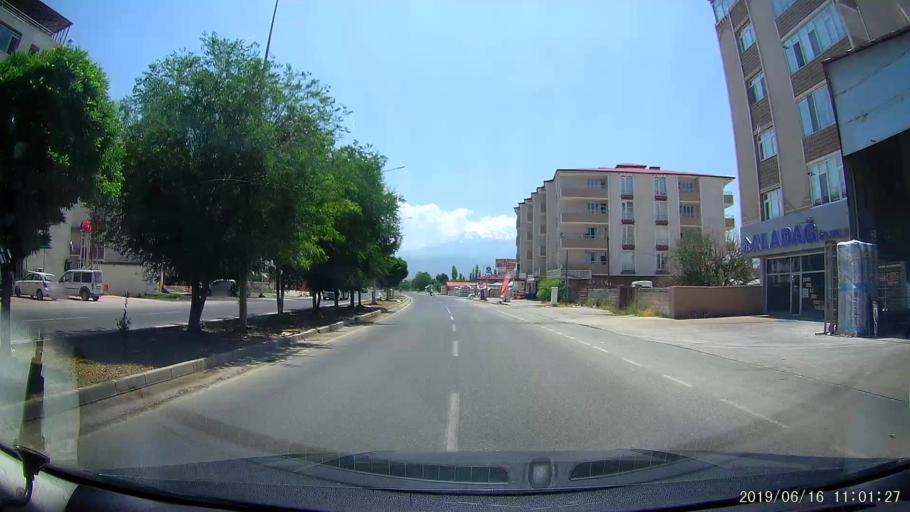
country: TR
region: Igdir
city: Igdir
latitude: 39.9149
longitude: 44.0498
